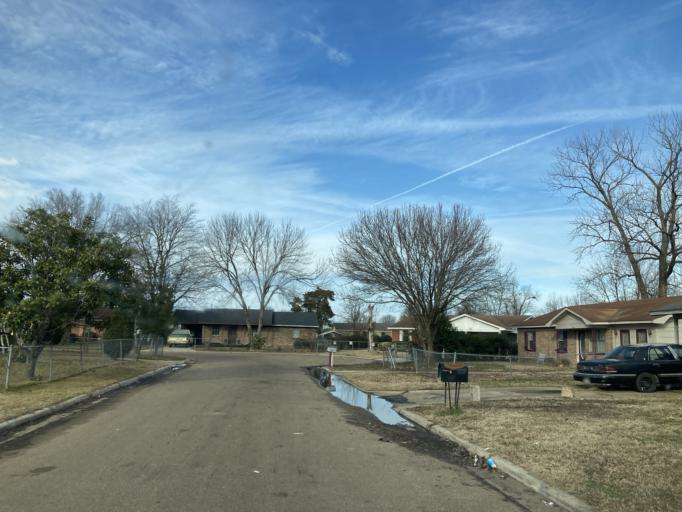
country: US
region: Mississippi
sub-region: Humphreys County
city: Belzoni
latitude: 33.1689
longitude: -90.5014
